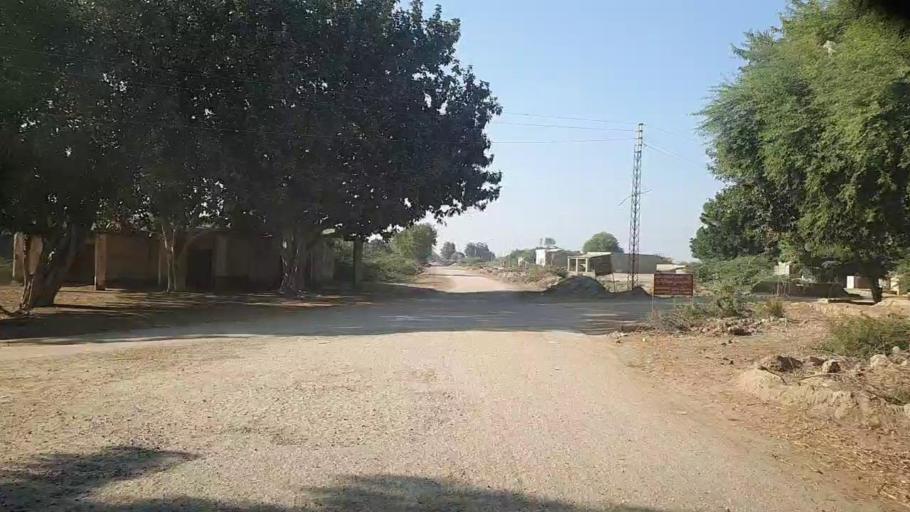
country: PK
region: Sindh
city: Darya Khan Marri
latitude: 26.6790
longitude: 68.3707
